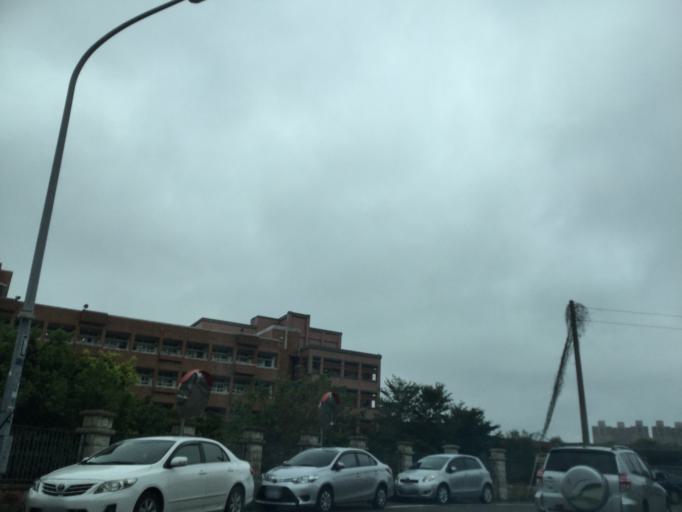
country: TW
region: Taiwan
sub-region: Hsinchu
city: Hsinchu
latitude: 24.7987
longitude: 121.0009
